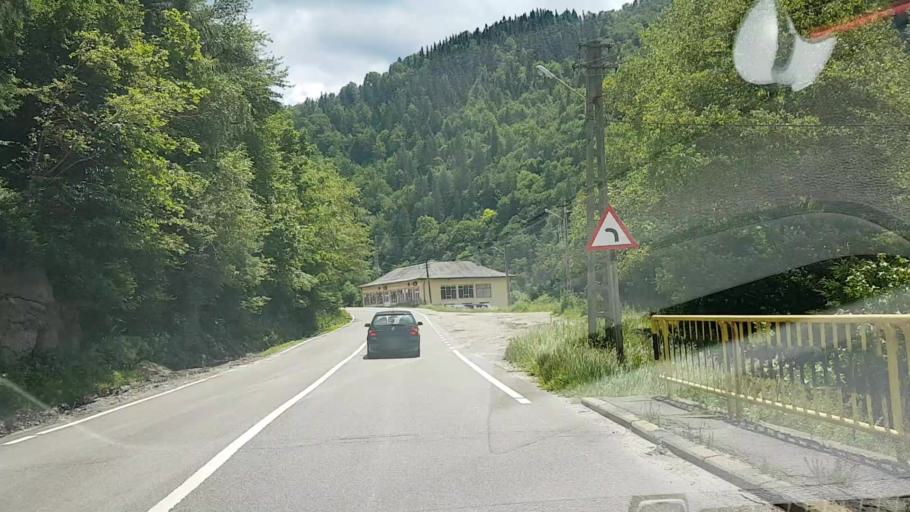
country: RO
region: Suceava
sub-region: Comuna Crucea
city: Crucea
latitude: 47.2848
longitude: 25.6363
